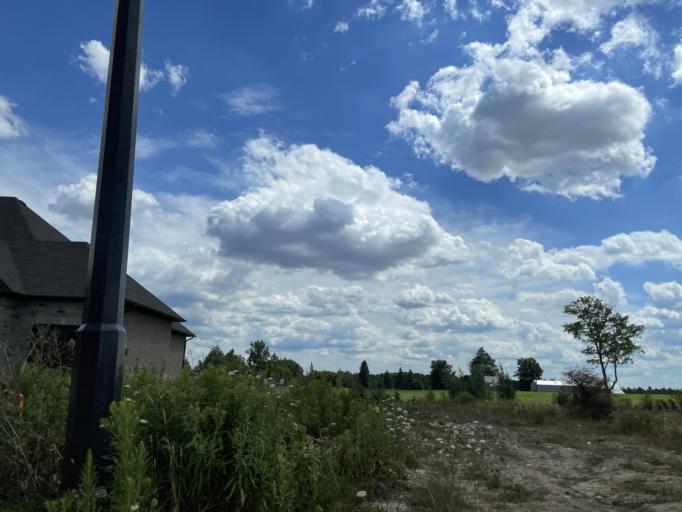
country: CA
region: Ontario
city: Waterloo
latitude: 43.5362
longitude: -80.3970
